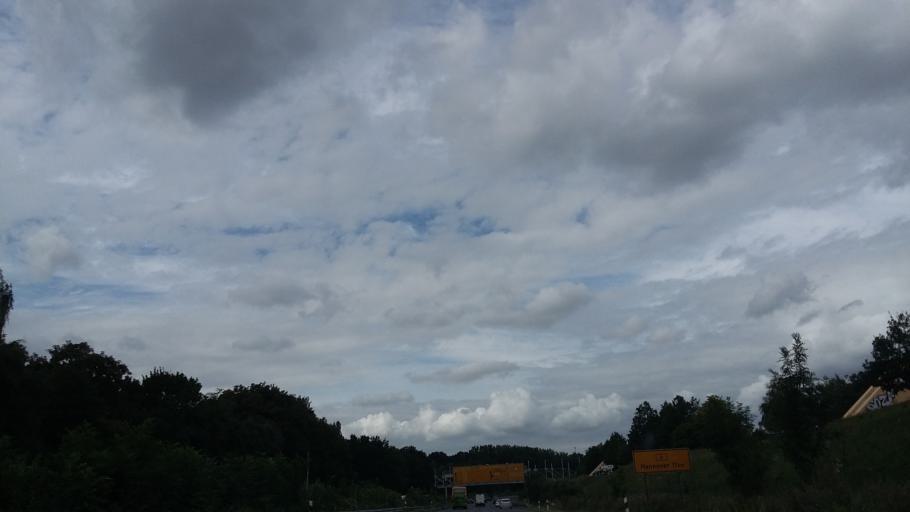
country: DE
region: Lower Saxony
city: Laatzen
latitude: 52.3099
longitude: 9.8208
